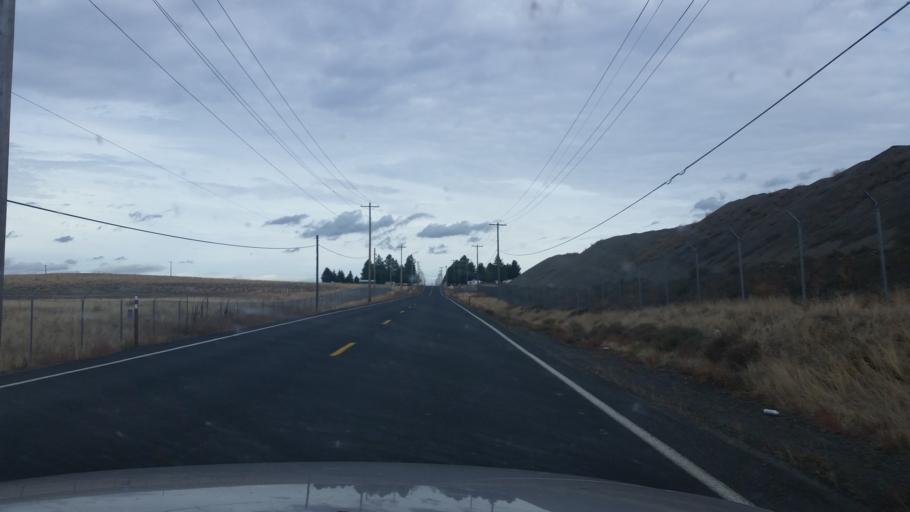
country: US
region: Washington
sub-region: Spokane County
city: Airway Heights
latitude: 47.6320
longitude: -117.6040
